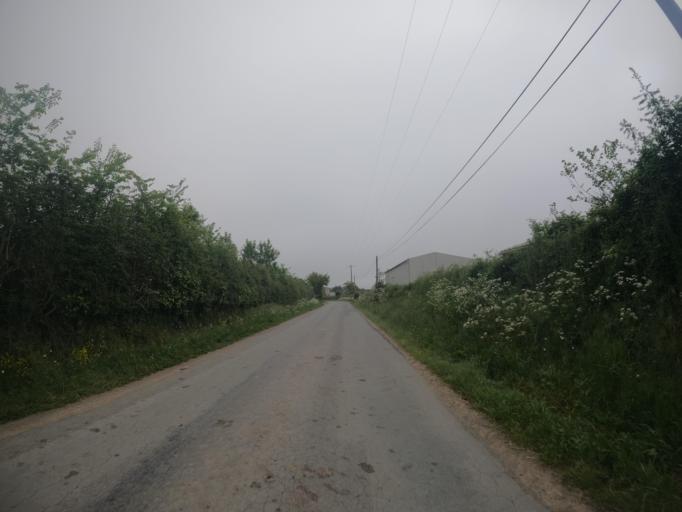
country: FR
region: Poitou-Charentes
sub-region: Departement des Deux-Sevres
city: Mauze-Thouarsais
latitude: 46.8977
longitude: -0.3401
